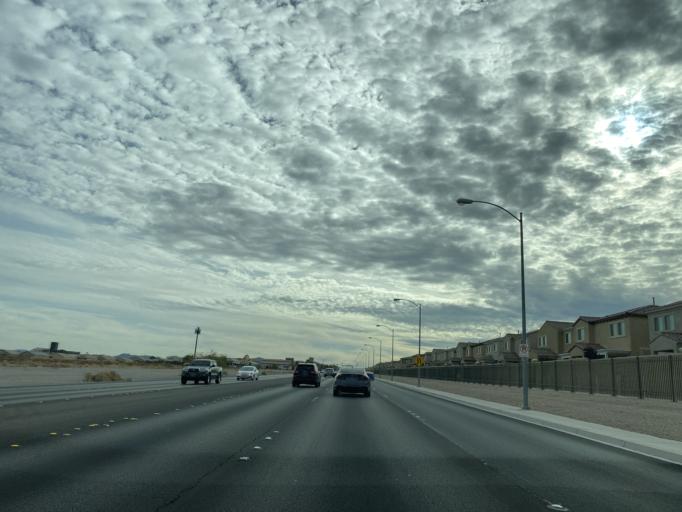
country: US
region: Nevada
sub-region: Clark County
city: Enterprise
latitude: 36.0459
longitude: -115.2792
